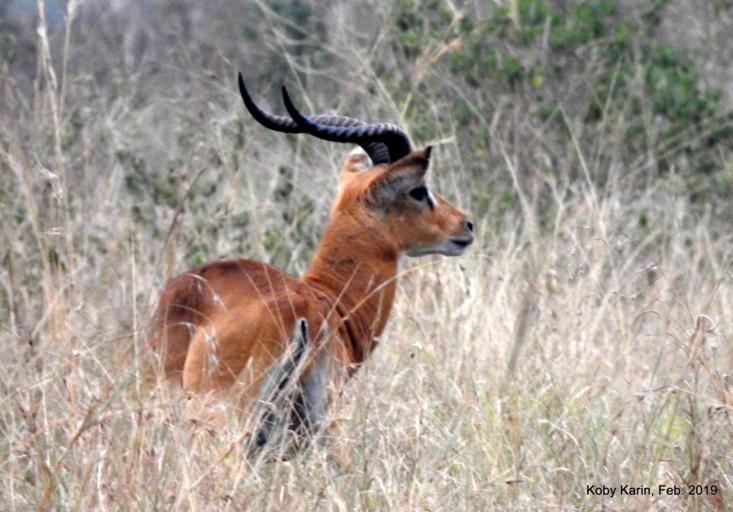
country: UG
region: Western Region
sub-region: Rubirizi District
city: Rubirizi
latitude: -0.0874
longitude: 30.0176
